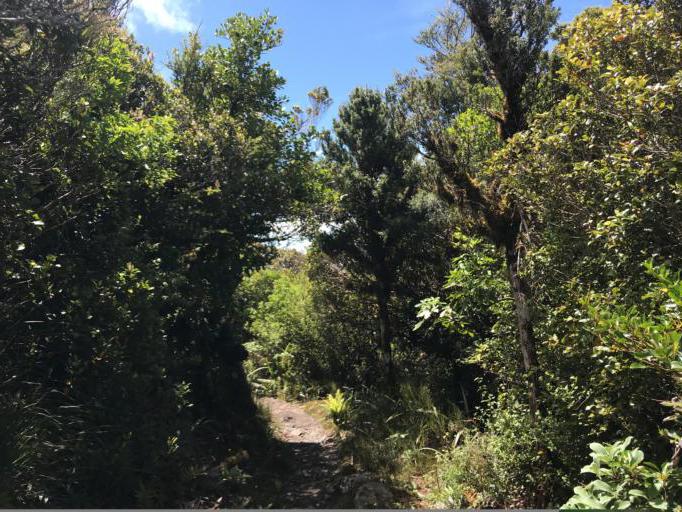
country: NZ
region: Wellington
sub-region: Kapiti Coast District
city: Otaki
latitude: -40.9093
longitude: 175.2589
